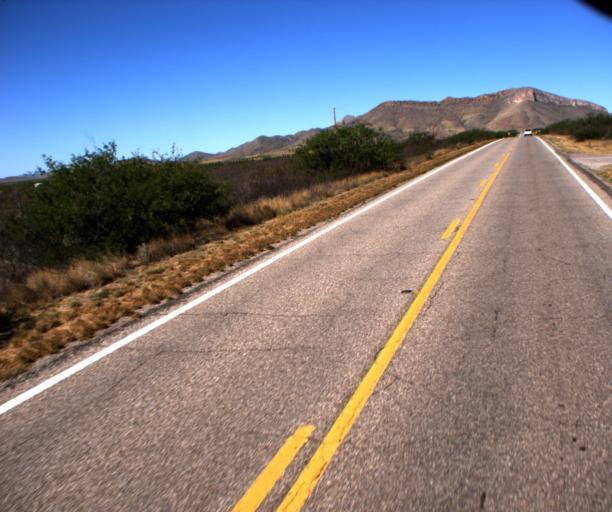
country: US
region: Arizona
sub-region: Cochise County
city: Huachuca City
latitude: 31.6920
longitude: -110.3869
